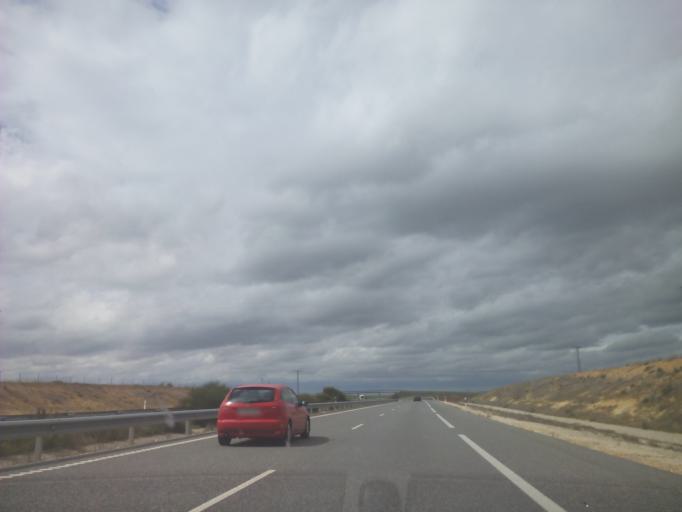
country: ES
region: Castille and Leon
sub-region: Provincia de Salamanca
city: Machacon
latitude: 40.9233
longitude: -5.5341
